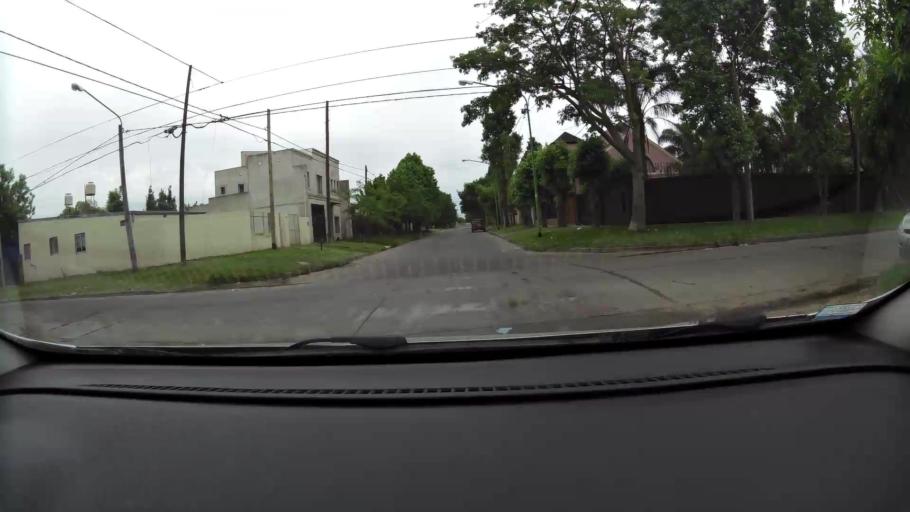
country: AR
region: Buenos Aires
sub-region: Partido de Campana
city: Campana
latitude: -34.1787
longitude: -58.9561
